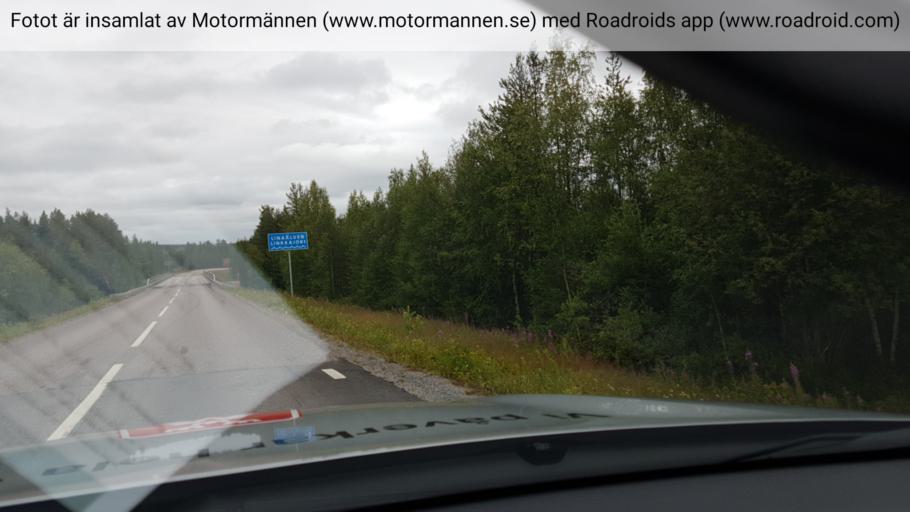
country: SE
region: Norrbotten
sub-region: Gallivare Kommun
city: Gaellivare
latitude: 67.0741
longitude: 21.3314
